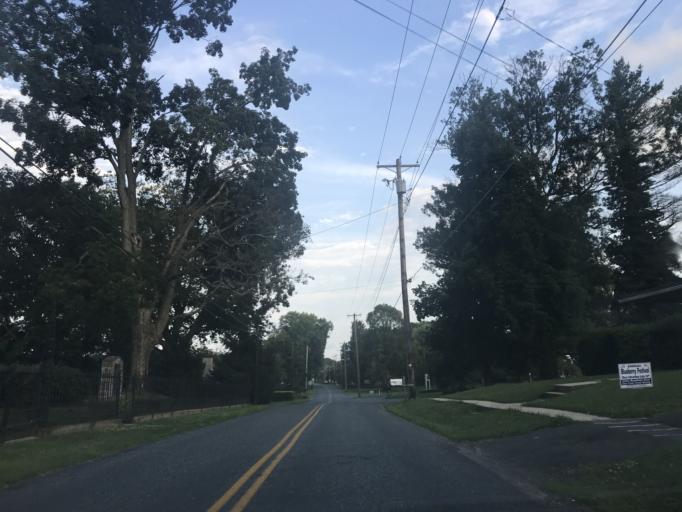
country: US
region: Maryland
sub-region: Harford County
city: Aberdeen
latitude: 39.6379
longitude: -76.2009
